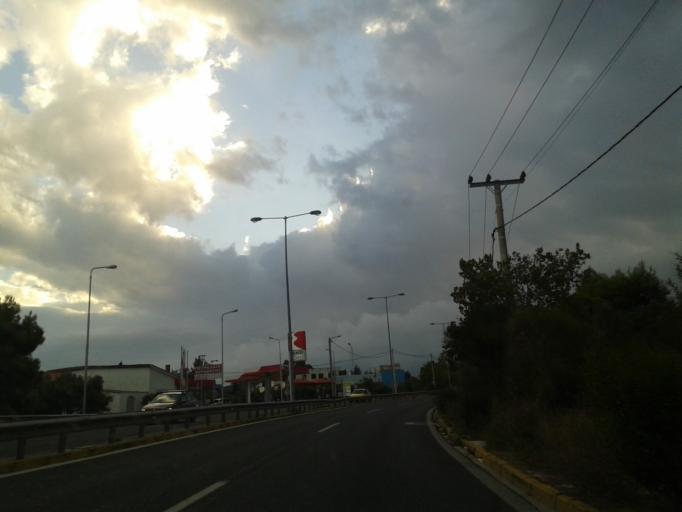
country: GR
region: Attica
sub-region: Nomarchia Anatolikis Attikis
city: Pikermi
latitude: 38.0058
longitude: 23.9542
